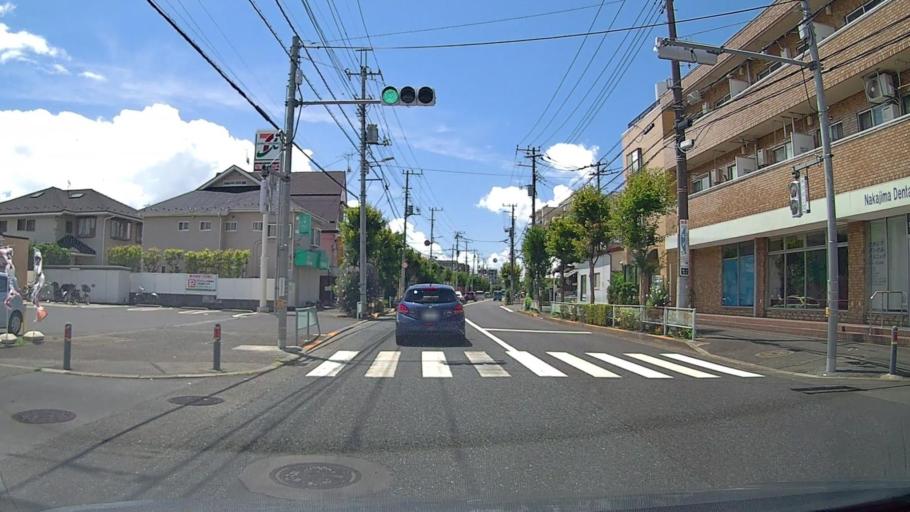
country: JP
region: Tokyo
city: Nishi-Tokyo-shi
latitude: 35.7420
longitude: 139.5658
